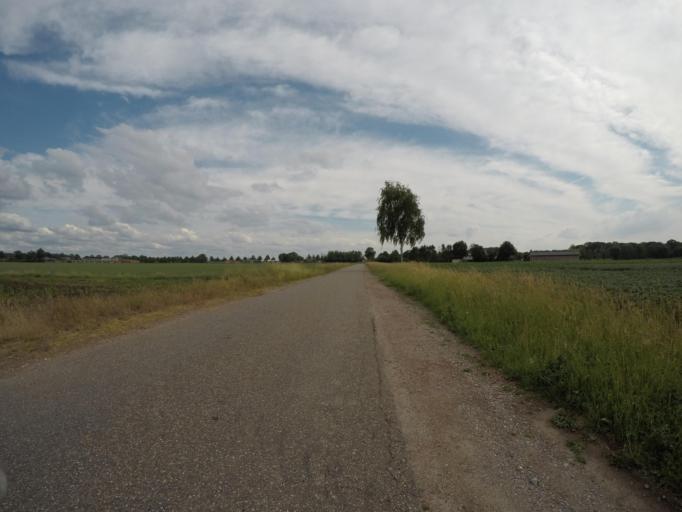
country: BE
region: Flanders
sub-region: Provincie Antwerpen
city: Hoogstraten
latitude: 51.3752
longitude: 4.7507
